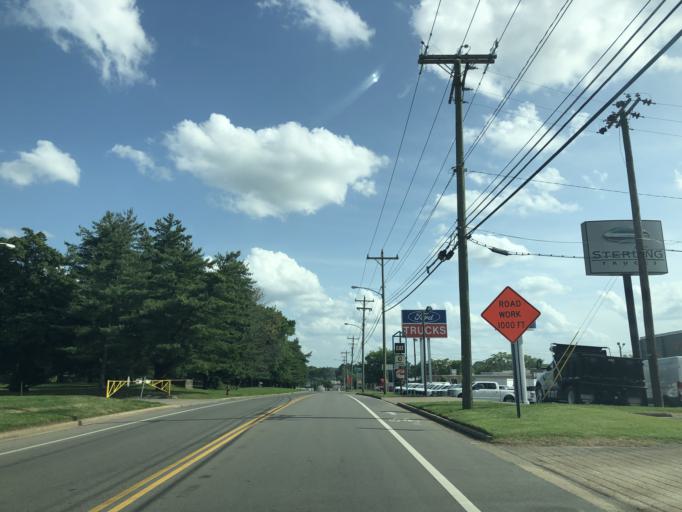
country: US
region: Tennessee
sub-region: Davidson County
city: Nashville
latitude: 36.1309
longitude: -86.7418
